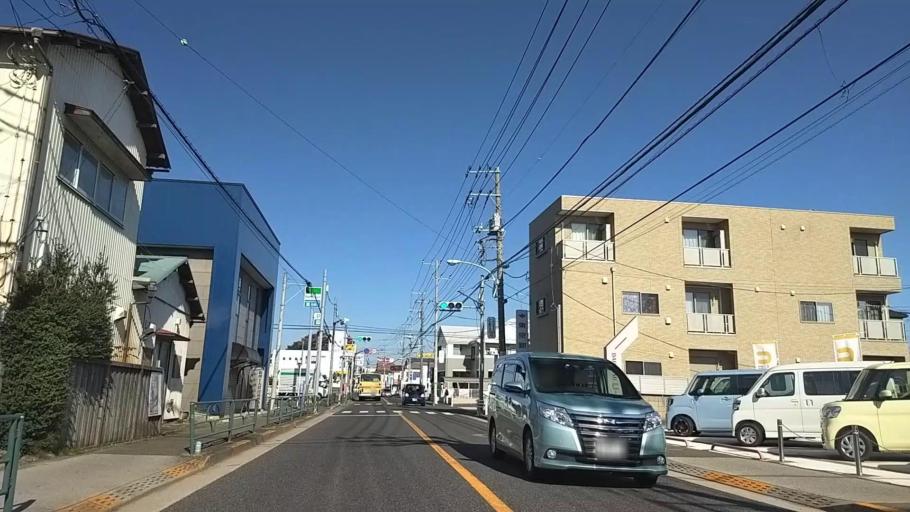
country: JP
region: Tokyo
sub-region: Machida-shi
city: Machida
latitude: 35.5301
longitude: 139.4622
